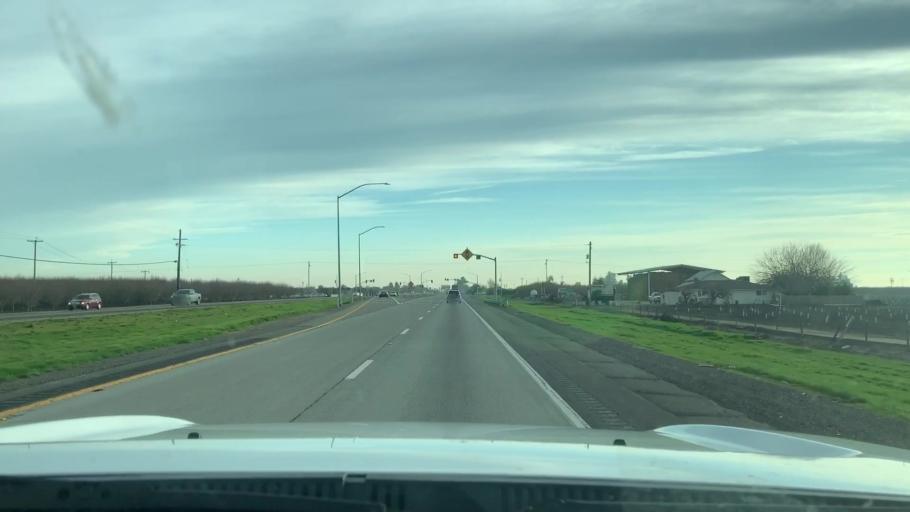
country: US
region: California
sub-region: Kings County
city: Lemoore
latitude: 36.3165
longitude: -119.8082
